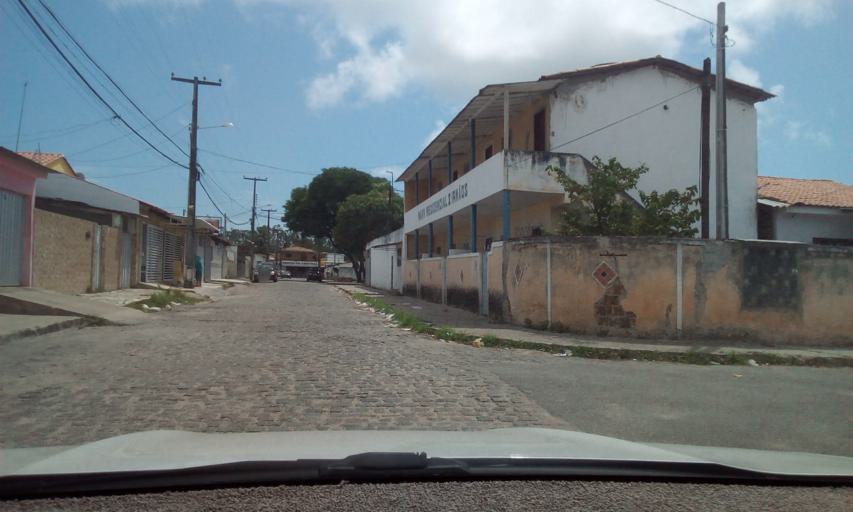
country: BR
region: Paraiba
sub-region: Joao Pessoa
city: Joao Pessoa
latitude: -7.1877
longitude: -34.8407
